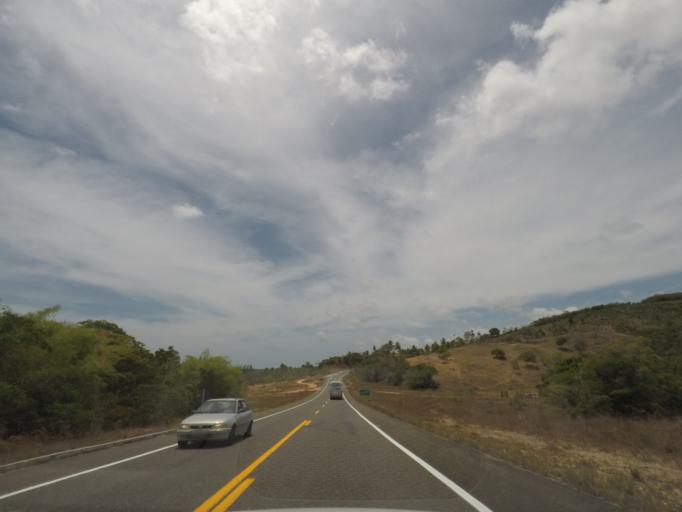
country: BR
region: Bahia
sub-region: Conde
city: Conde
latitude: -11.7684
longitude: -37.5911
